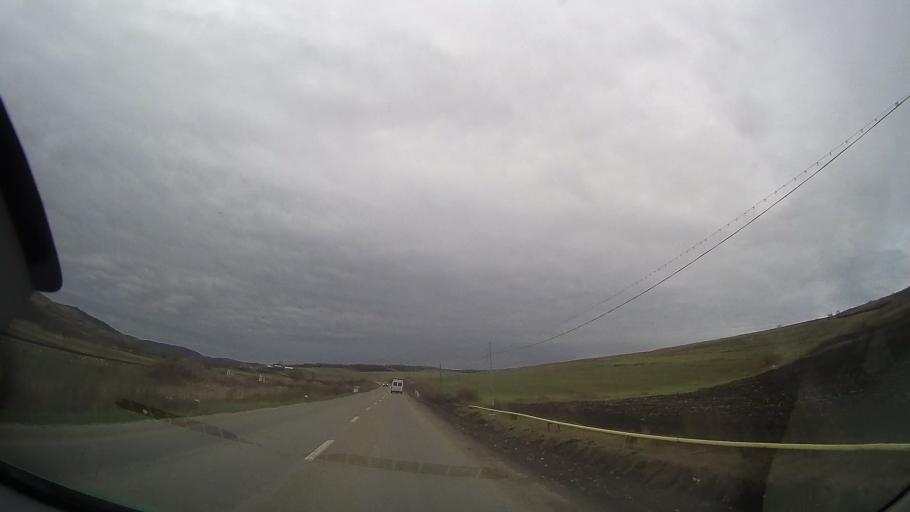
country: RO
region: Cluj
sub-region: Comuna Catina
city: Catina
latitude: 46.8087
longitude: 24.2193
